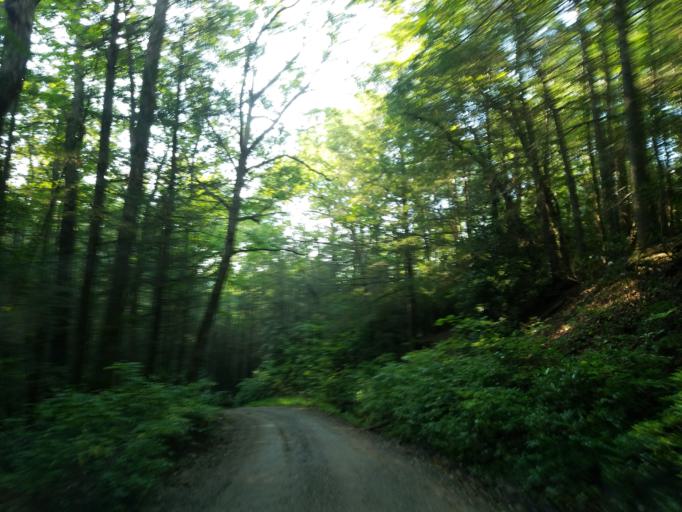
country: US
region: Georgia
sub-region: Lumpkin County
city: Dahlonega
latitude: 34.6587
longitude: -84.0868
